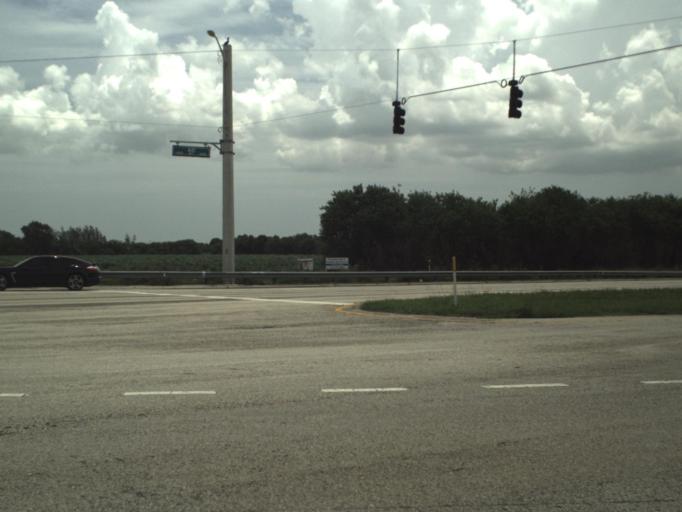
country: US
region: Florida
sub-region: Palm Beach County
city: Villages of Oriole
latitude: 26.4538
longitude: -80.2047
